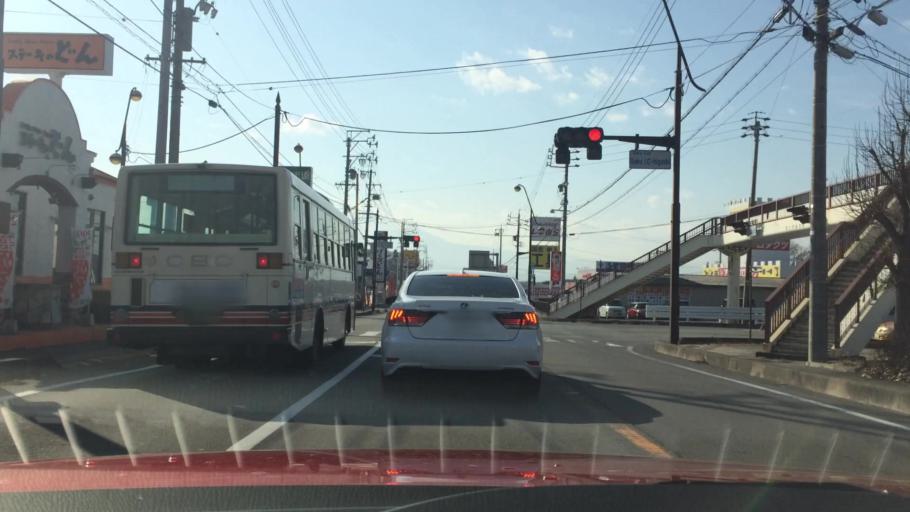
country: JP
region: Nagano
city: Komoro
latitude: 36.2835
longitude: 138.4830
